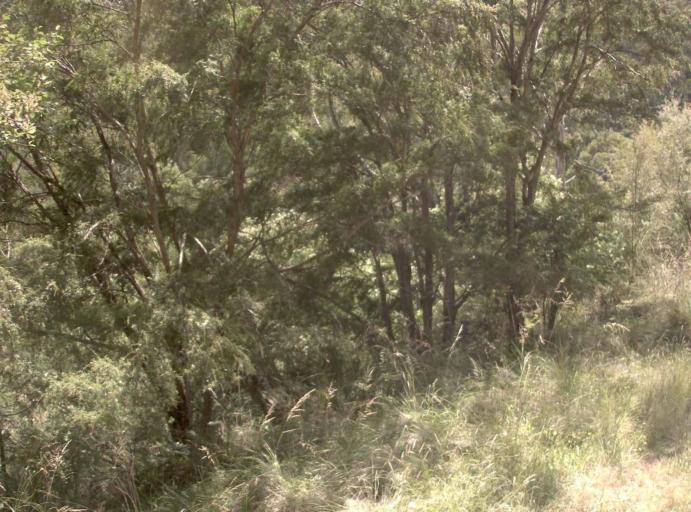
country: AU
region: Victoria
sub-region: Latrobe
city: Traralgon
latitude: -37.9311
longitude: 146.4495
